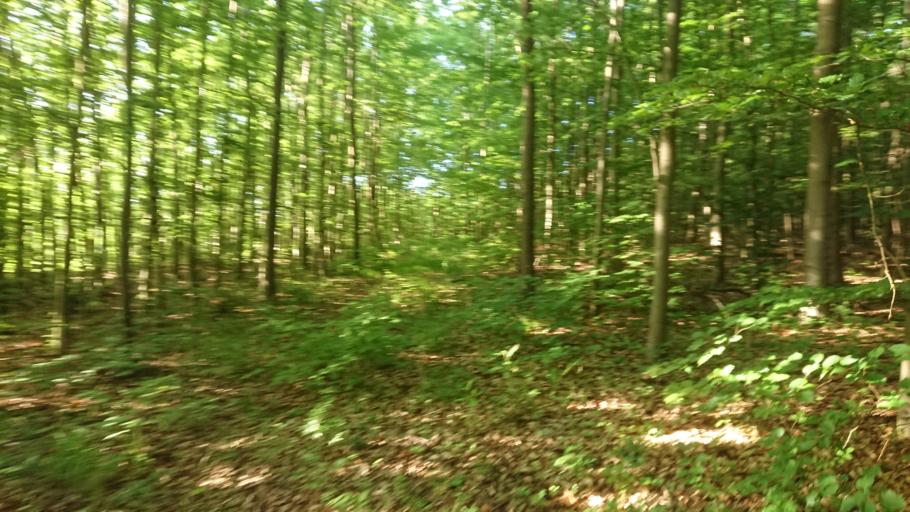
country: DE
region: Lower Saxony
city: Hardegsen
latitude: 51.6027
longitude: 9.8384
